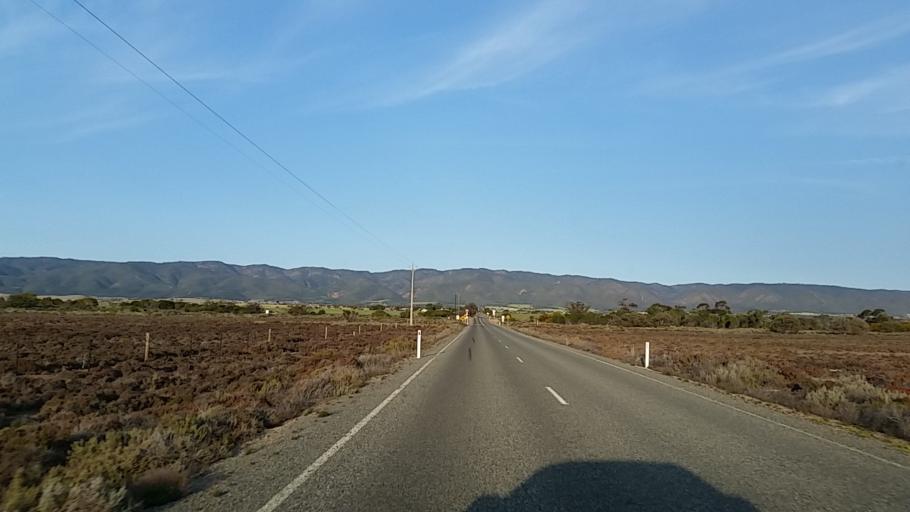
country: AU
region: South Australia
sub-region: Port Pirie City and Dists
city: Port Pirie
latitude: -33.1040
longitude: 138.0524
